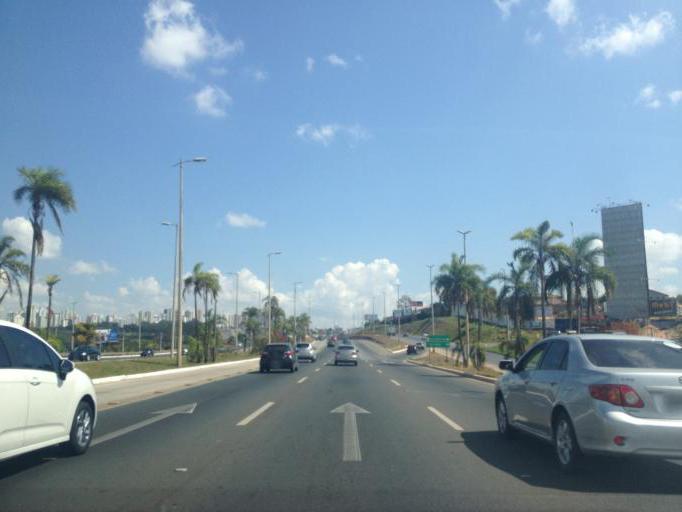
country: BR
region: Federal District
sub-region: Brasilia
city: Brasilia
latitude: -15.8179
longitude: -48.0146
